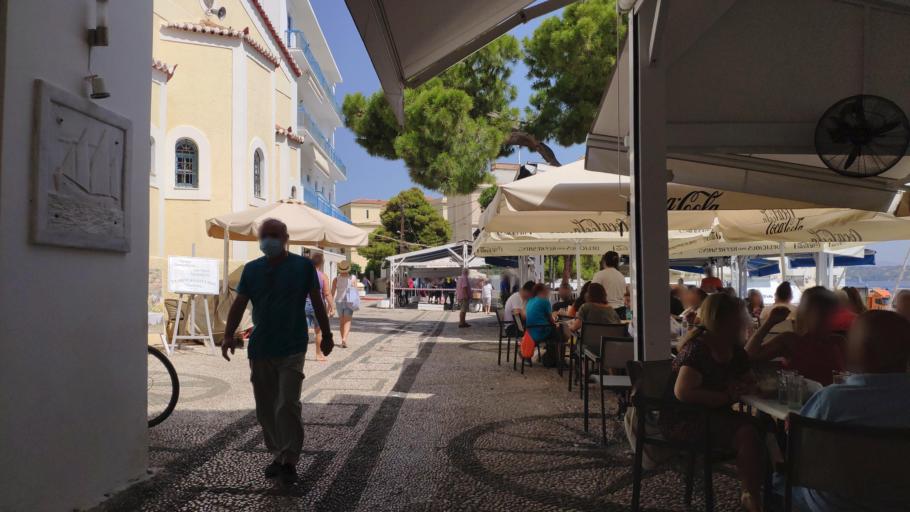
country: GR
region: Attica
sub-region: Nomos Piraios
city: Spetses
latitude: 37.2676
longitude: 23.1555
